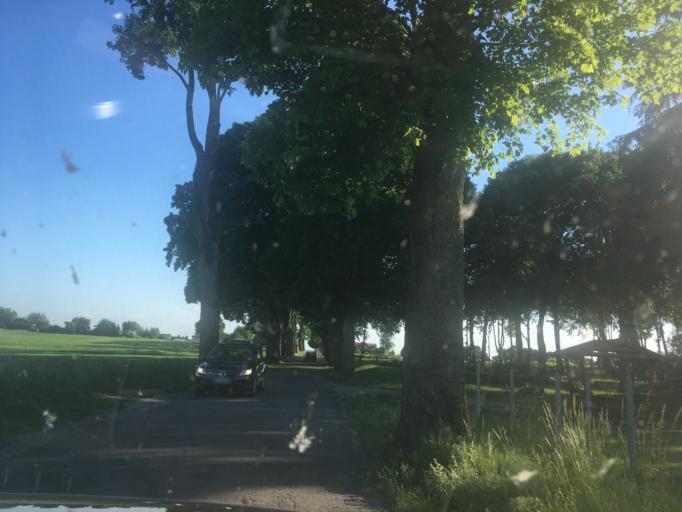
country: PL
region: Warmian-Masurian Voivodeship
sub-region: Powiat ostrodzki
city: Ostroda
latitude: 53.6795
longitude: 20.0516
